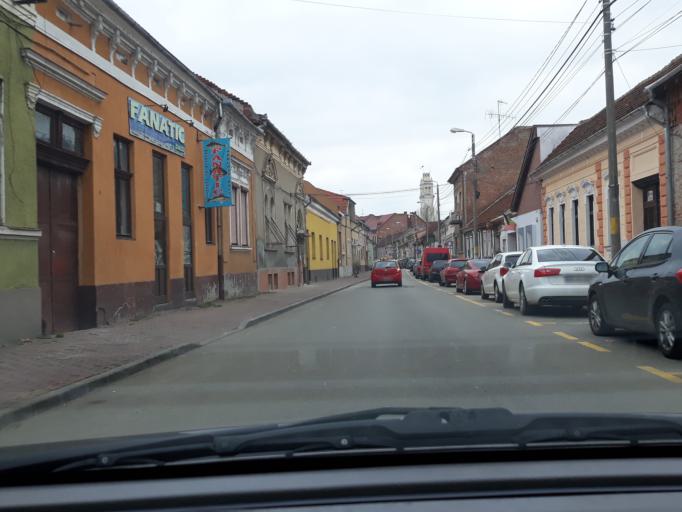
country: RO
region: Bihor
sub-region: Comuna Biharea
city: Oradea
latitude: 47.0600
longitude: 21.9276
